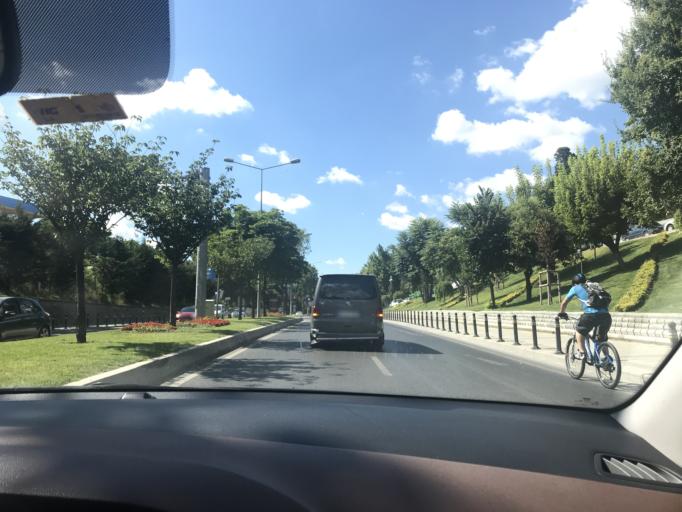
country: TR
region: Istanbul
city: UEskuedar
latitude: 41.0082
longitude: 29.0237
